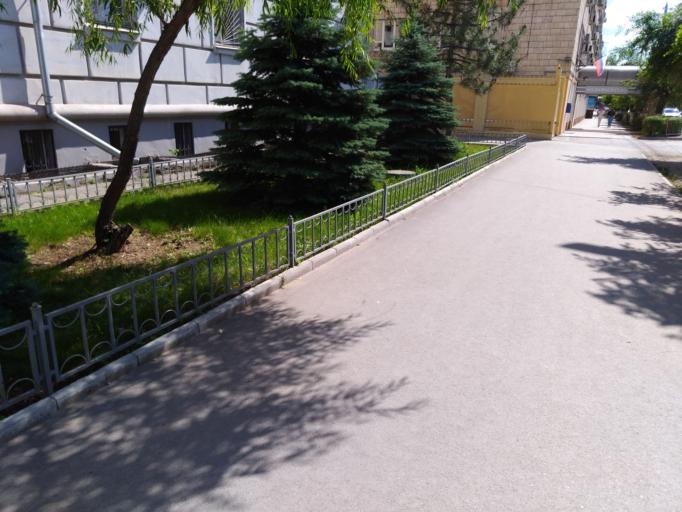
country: RU
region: Volgograd
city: Volgograd
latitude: 48.7143
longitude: 44.5206
